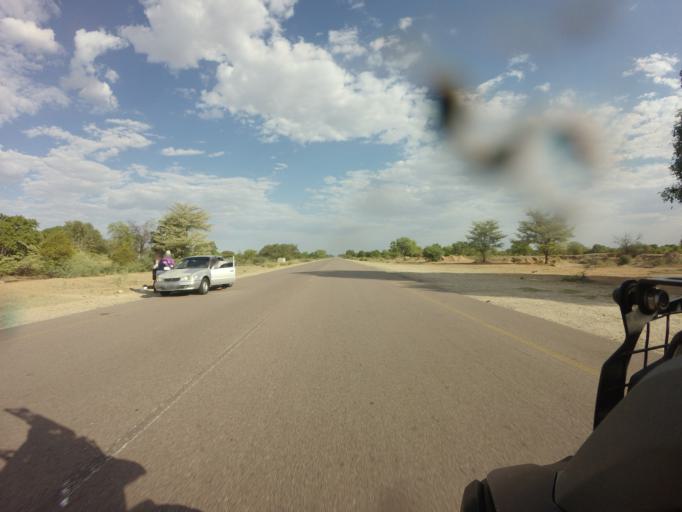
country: AO
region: Cunene
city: Ondjiva
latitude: -16.9753
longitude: 15.6099
